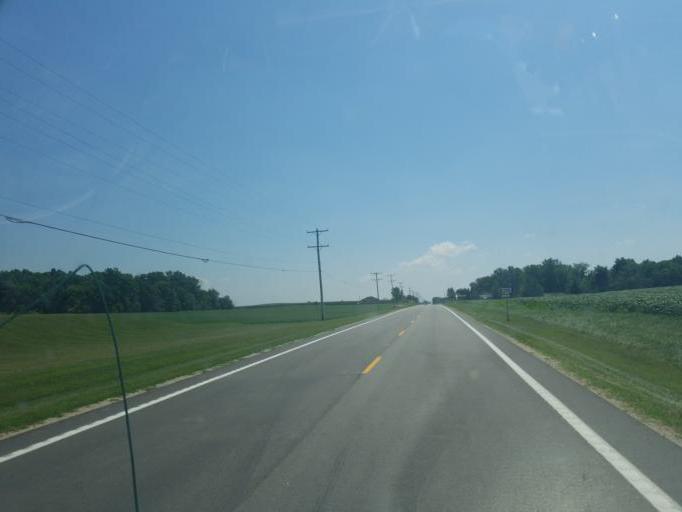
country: US
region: Ohio
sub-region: Shelby County
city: Botkins
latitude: 40.4822
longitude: -84.1840
